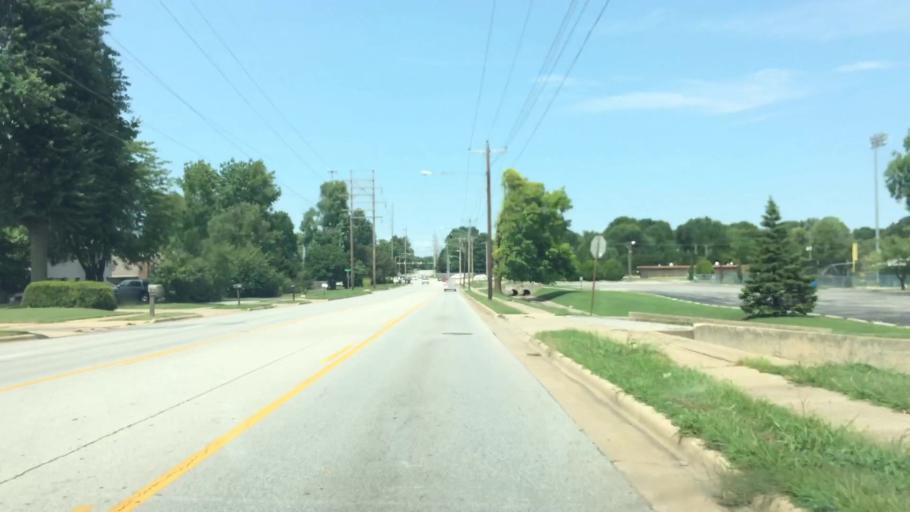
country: US
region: Missouri
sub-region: Greene County
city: Springfield
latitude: 37.1643
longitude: -93.2716
